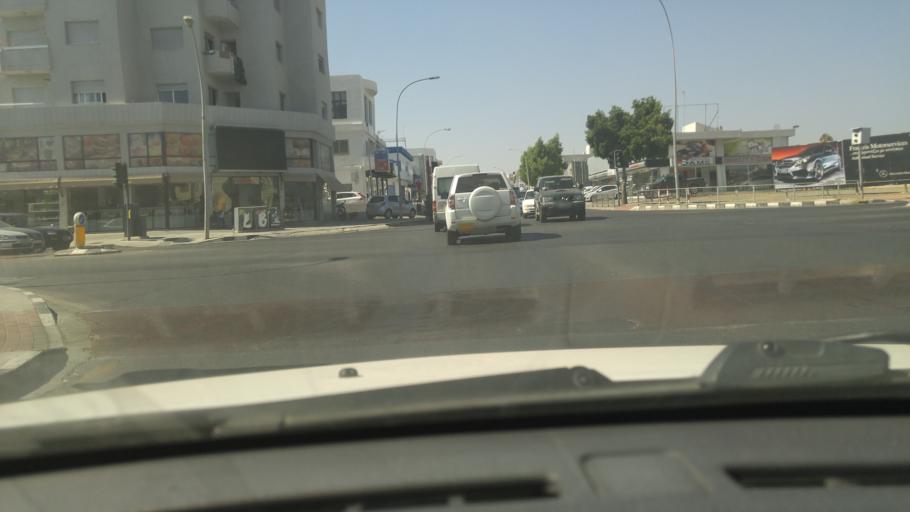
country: CY
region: Limassol
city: Limassol
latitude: 34.6752
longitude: 33.0117
